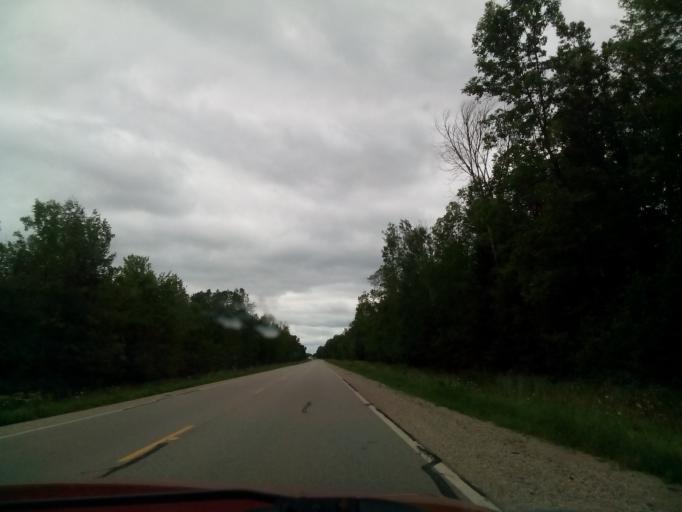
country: US
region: Wisconsin
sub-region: Menominee County
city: Legend Lake
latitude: 44.9775
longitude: -88.4485
